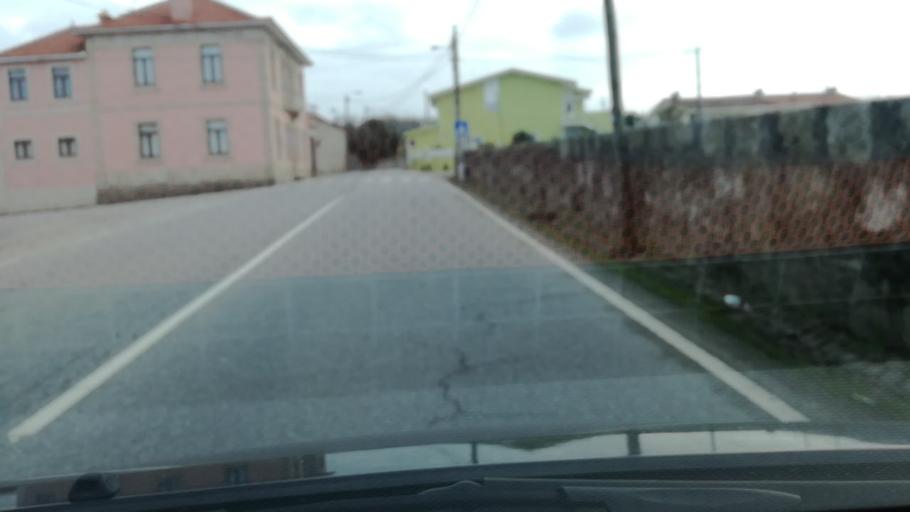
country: PT
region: Porto
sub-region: Maia
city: Gemunde
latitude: 41.2654
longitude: -8.6495
